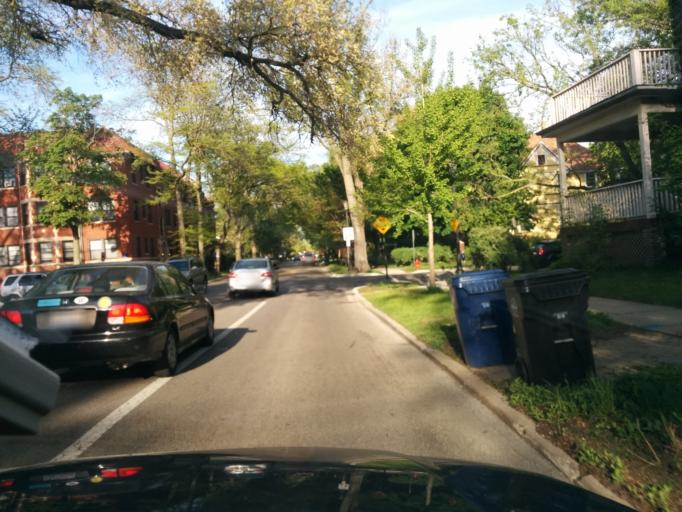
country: US
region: Illinois
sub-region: Cook County
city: Evanston
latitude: 42.0412
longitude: -87.6874
